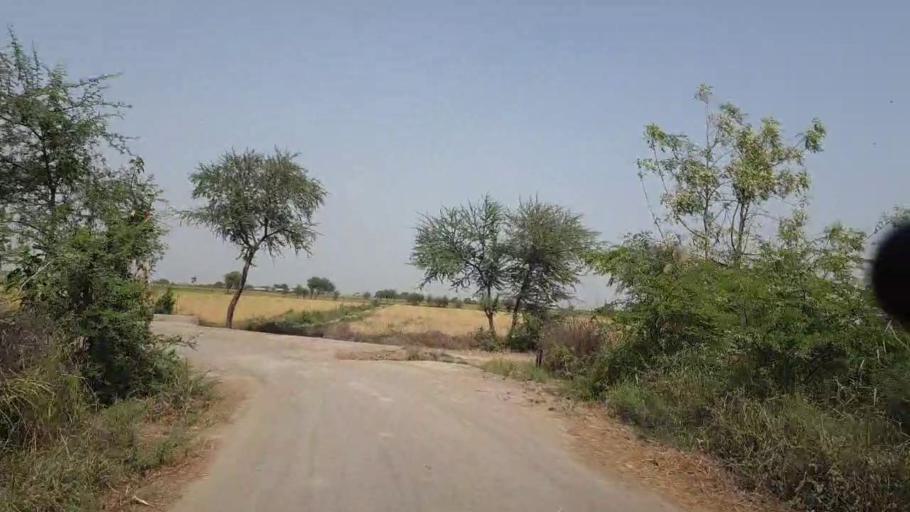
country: PK
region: Sindh
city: Matli
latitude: 25.0631
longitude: 68.6923
